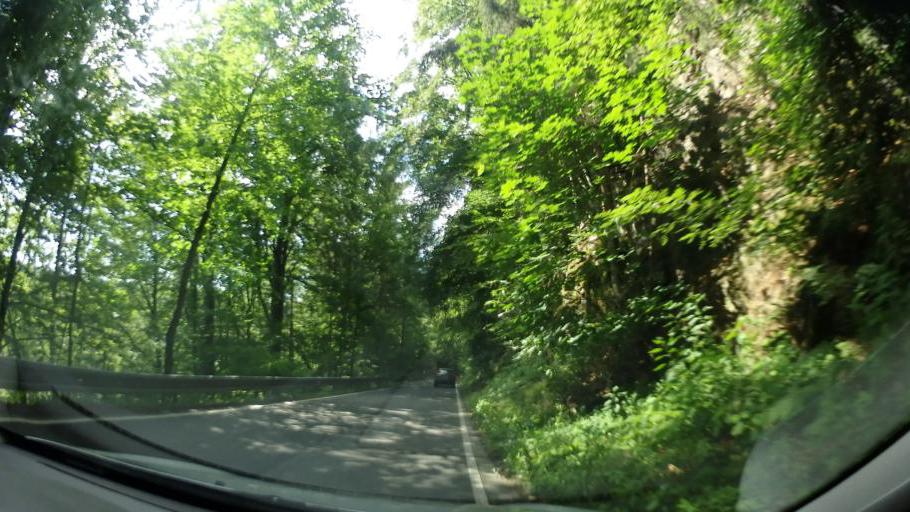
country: CZ
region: Olomoucky
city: Zabreh
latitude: 49.8646
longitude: 16.8282
